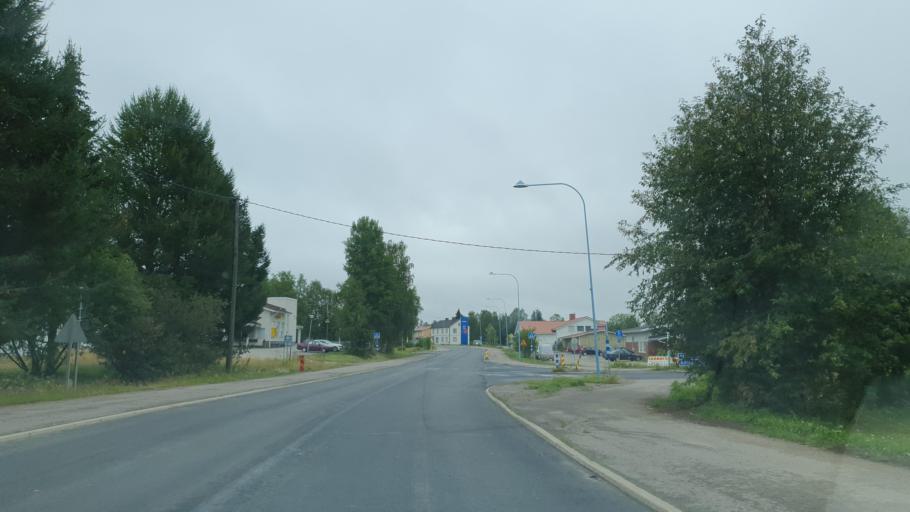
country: FI
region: Lapland
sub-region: Itae-Lappi
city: Pelkosenniemi
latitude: 67.1079
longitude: 27.5139
